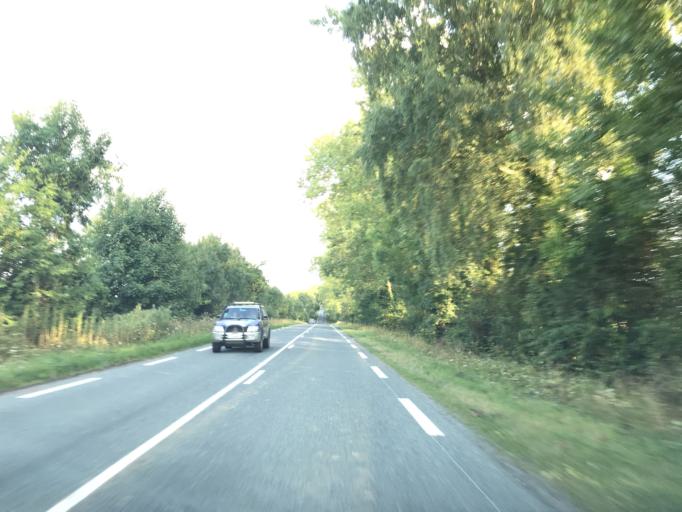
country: FR
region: Haute-Normandie
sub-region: Departement de la Seine-Maritime
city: La Cerlangue
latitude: 49.5032
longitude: 0.4230
